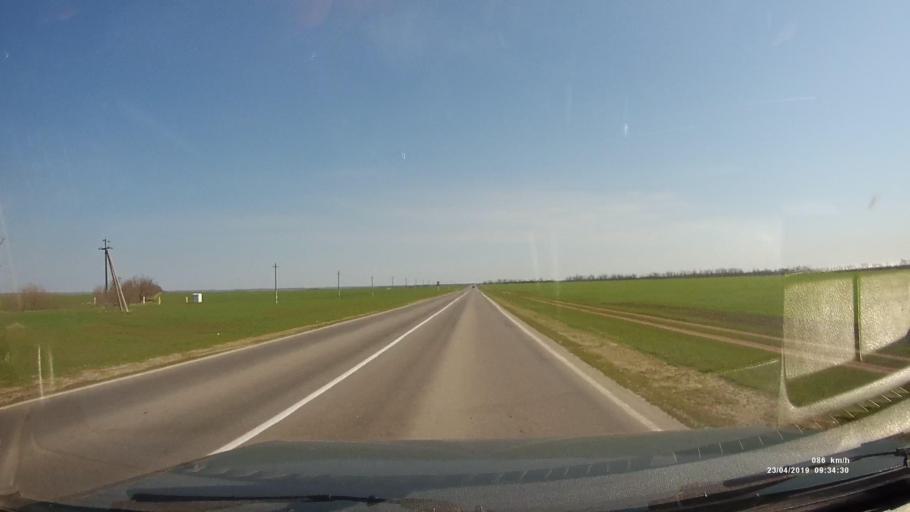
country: RU
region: Rostov
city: Gundorovskiy
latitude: 46.8121
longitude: 41.8594
